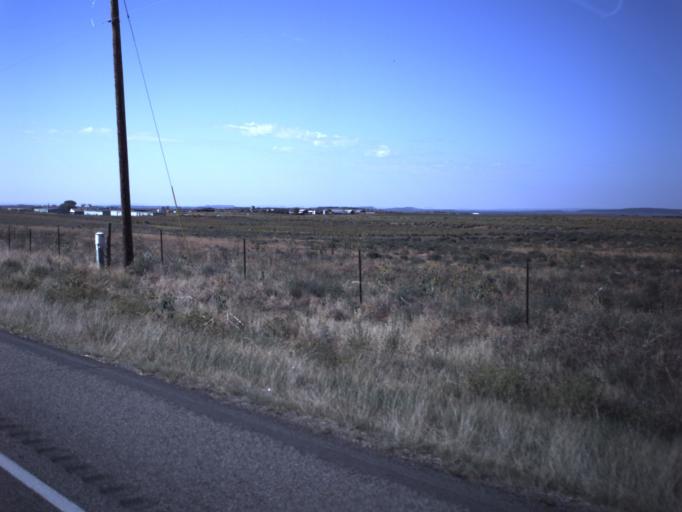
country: US
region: Utah
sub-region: San Juan County
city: Blanding
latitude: 37.5885
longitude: -109.4783
